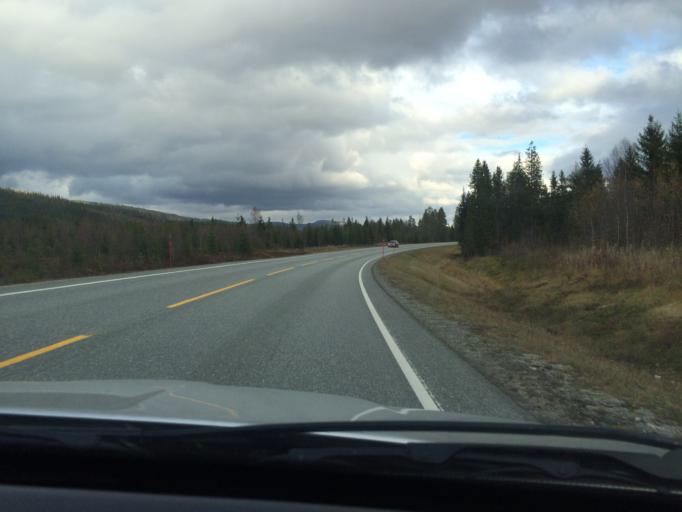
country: NO
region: Nord-Trondelag
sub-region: Namsskogan
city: Namsskogan
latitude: 64.7701
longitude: 12.8714
